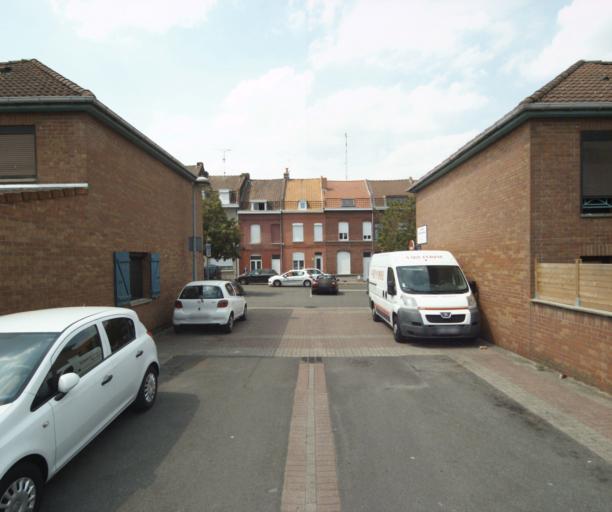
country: FR
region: Nord-Pas-de-Calais
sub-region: Departement du Nord
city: Tourcoing
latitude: 50.7272
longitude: 3.1469
